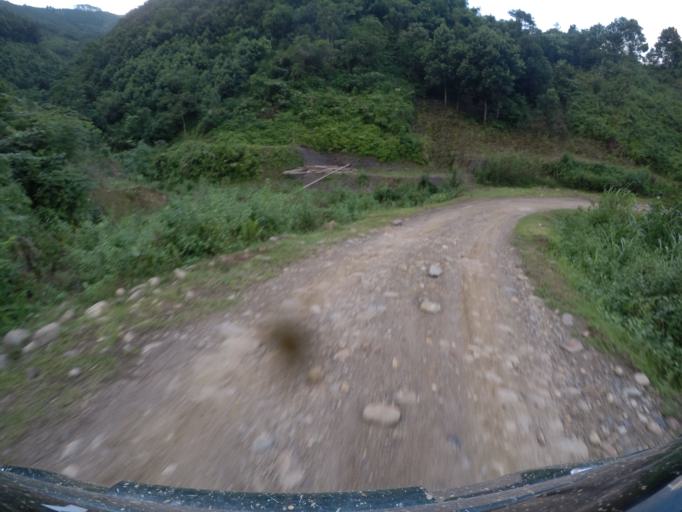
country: VN
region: Yen Bai
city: Son Thinh
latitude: 21.6992
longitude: 104.6310
